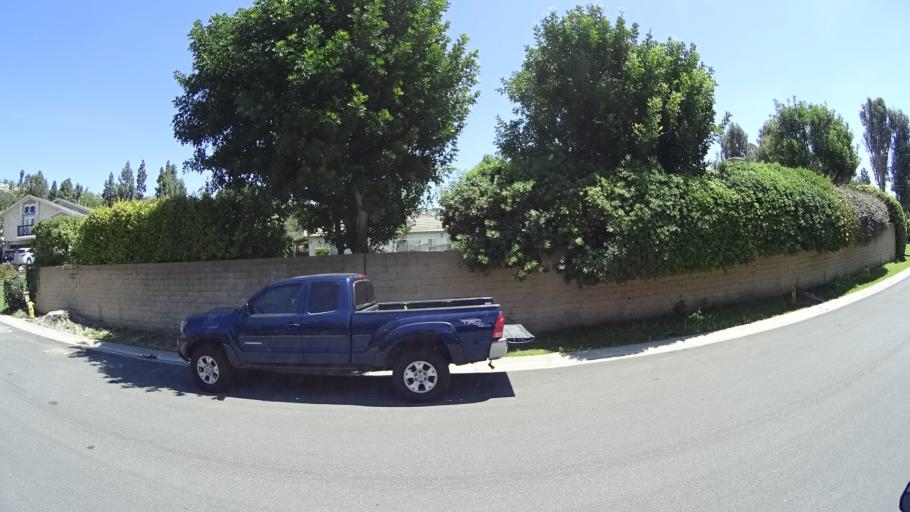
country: US
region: California
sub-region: Orange County
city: Villa Park
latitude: 33.8285
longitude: -117.7991
